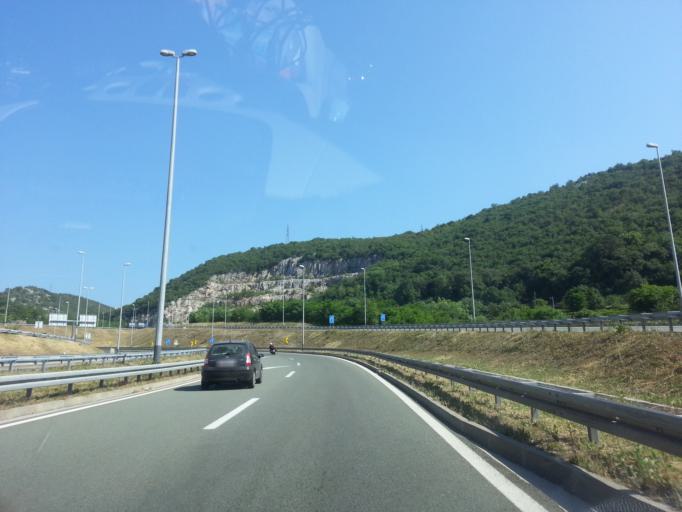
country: HR
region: Primorsko-Goranska
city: Cavle
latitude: 45.3354
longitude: 14.4728
